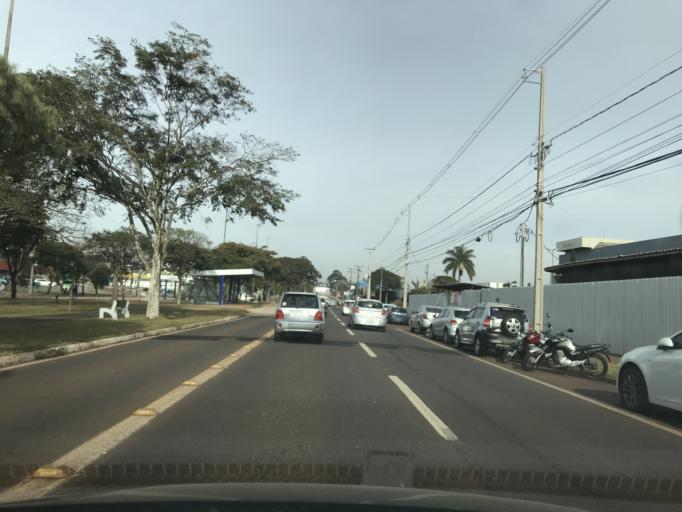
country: BR
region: Parana
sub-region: Cascavel
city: Cascavel
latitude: -24.9695
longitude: -53.4867
